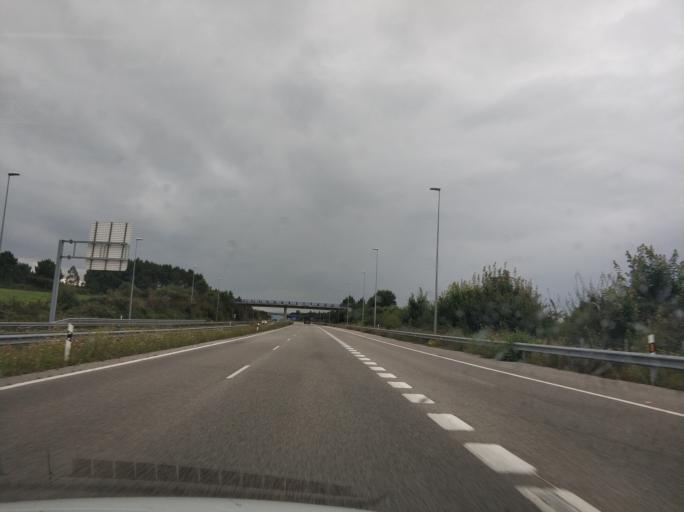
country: ES
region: Asturias
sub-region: Province of Asturias
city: Tapia de Casariego
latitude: 43.5466
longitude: -6.9189
